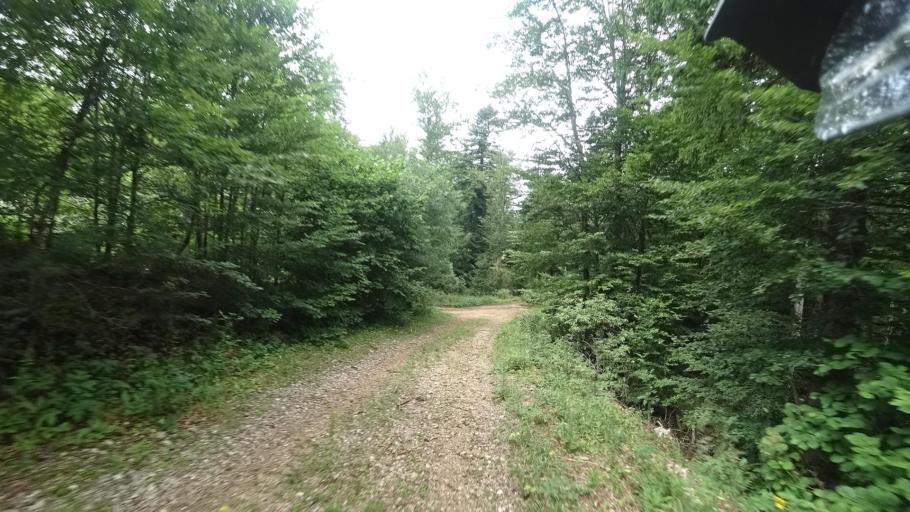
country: BA
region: Federation of Bosnia and Herzegovina
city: Bihac
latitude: 44.6298
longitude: 15.7924
